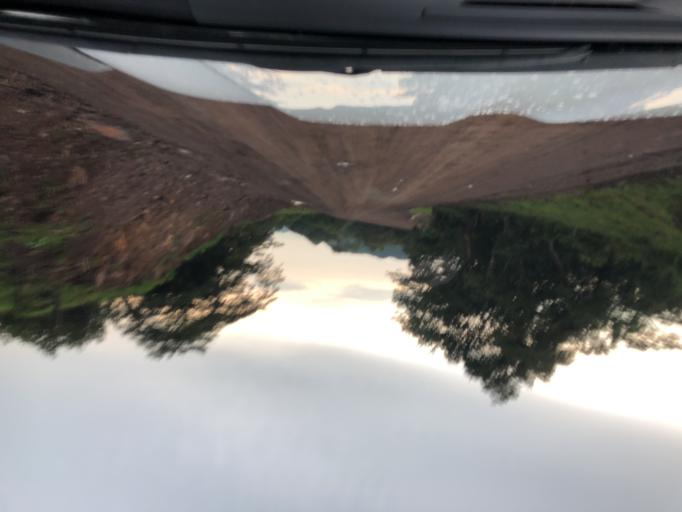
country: NI
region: Chontales
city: La Libertad
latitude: 12.1949
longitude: -85.1777
